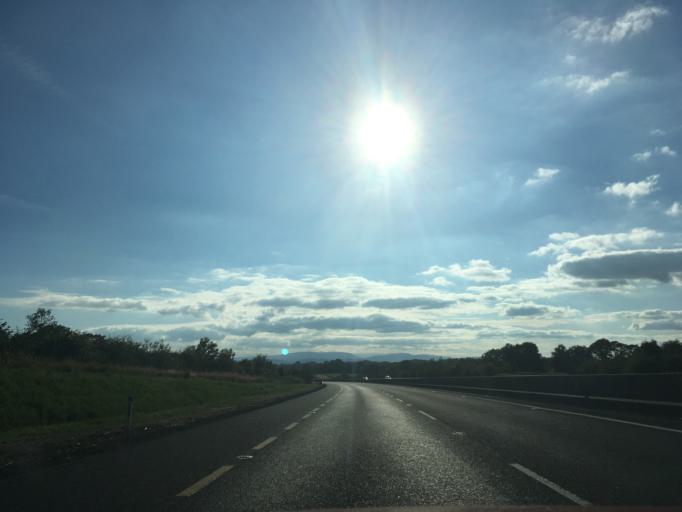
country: IE
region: Munster
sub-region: Waterford
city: Waterford
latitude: 52.2901
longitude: -7.1117
